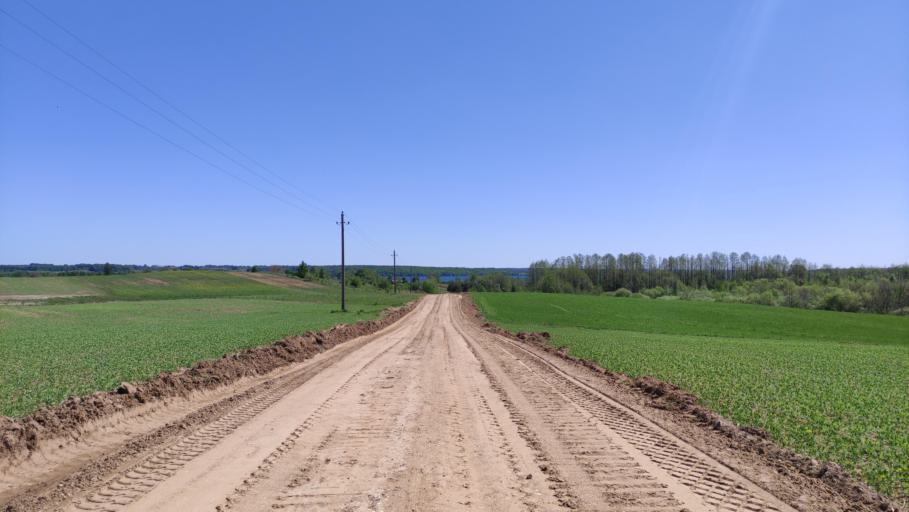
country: LT
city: Simnas
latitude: 54.3127
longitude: 23.8083
